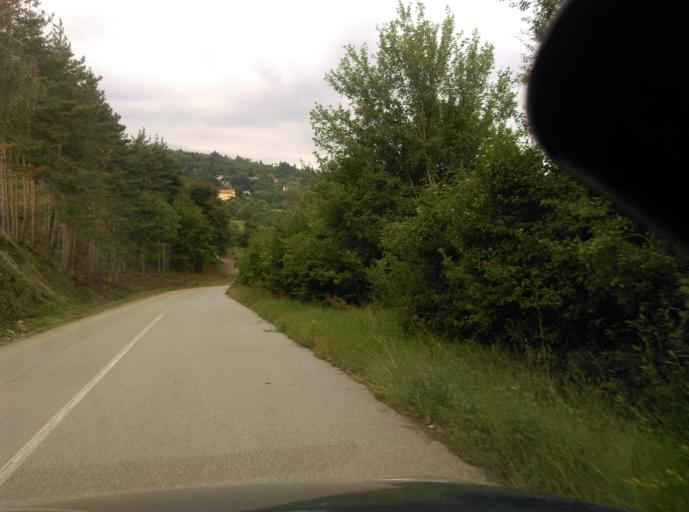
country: BG
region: Sofia-Capital
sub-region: Stolichna Obshtina
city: Sofia
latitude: 42.5914
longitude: 23.4044
